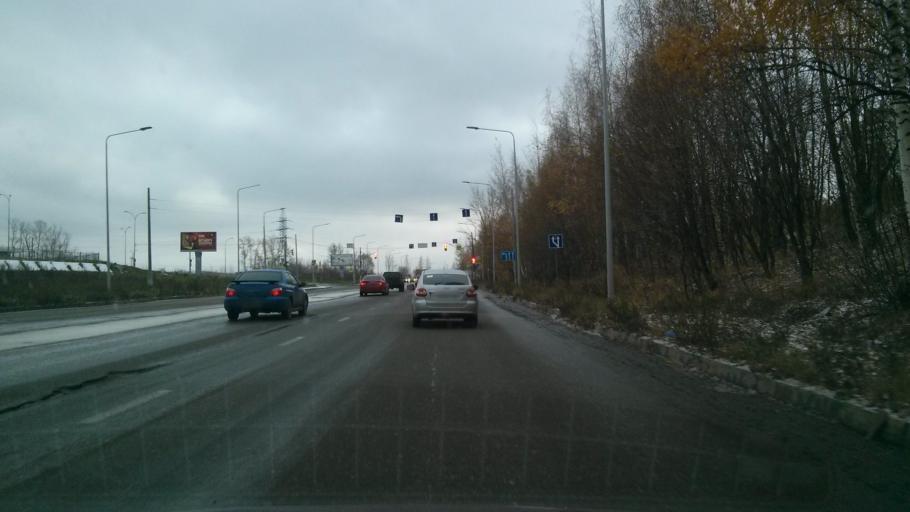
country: RU
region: Nizjnij Novgorod
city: Nizhniy Novgorod
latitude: 56.2680
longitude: 44.0234
